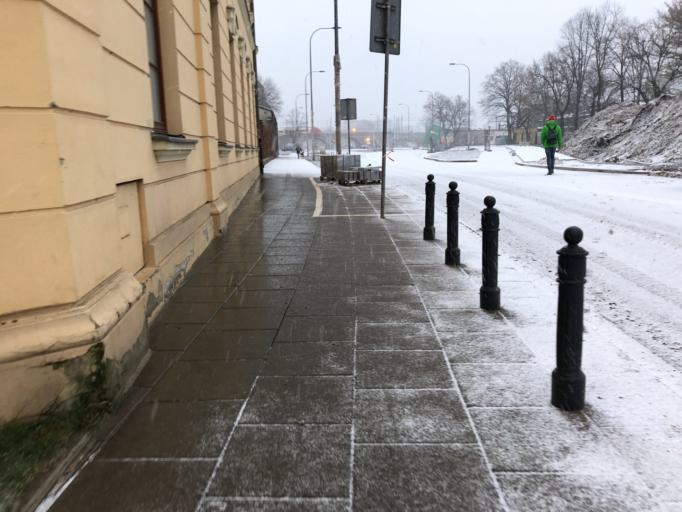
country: PL
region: Masovian Voivodeship
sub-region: Warszawa
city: Praga Polnoc
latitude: 52.2481
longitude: 21.0403
